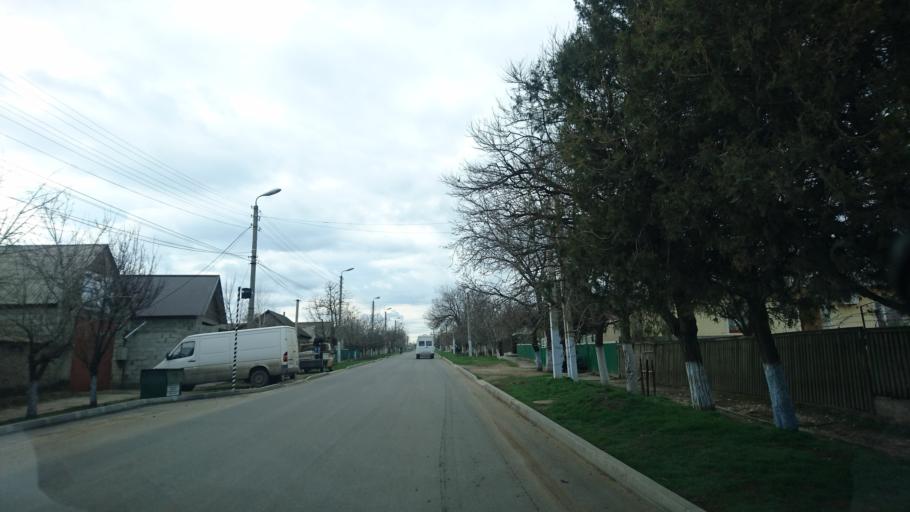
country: MD
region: Gagauzia
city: Comrat
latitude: 46.3026
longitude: 28.6431
